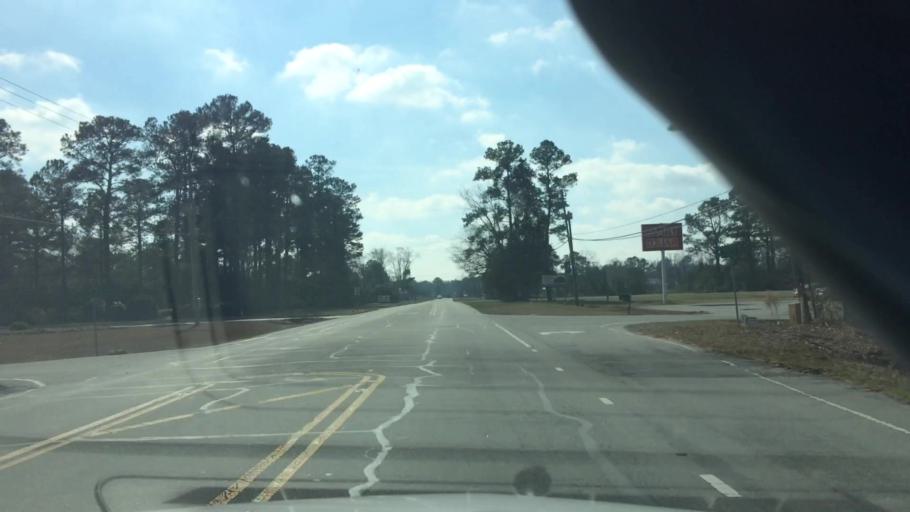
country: US
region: North Carolina
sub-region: Duplin County
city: Beulaville
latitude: 35.0689
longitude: -77.7372
